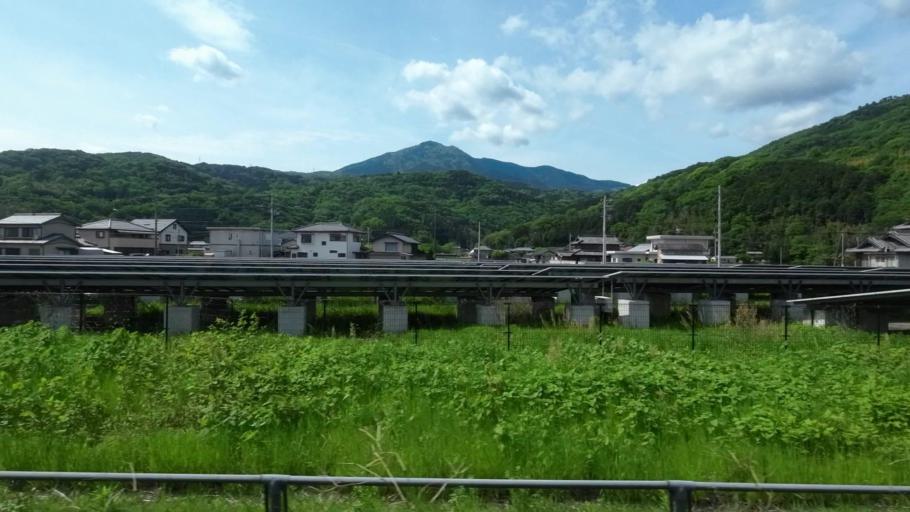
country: JP
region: Tokushima
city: Wakimachi
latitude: 34.0613
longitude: 134.2041
